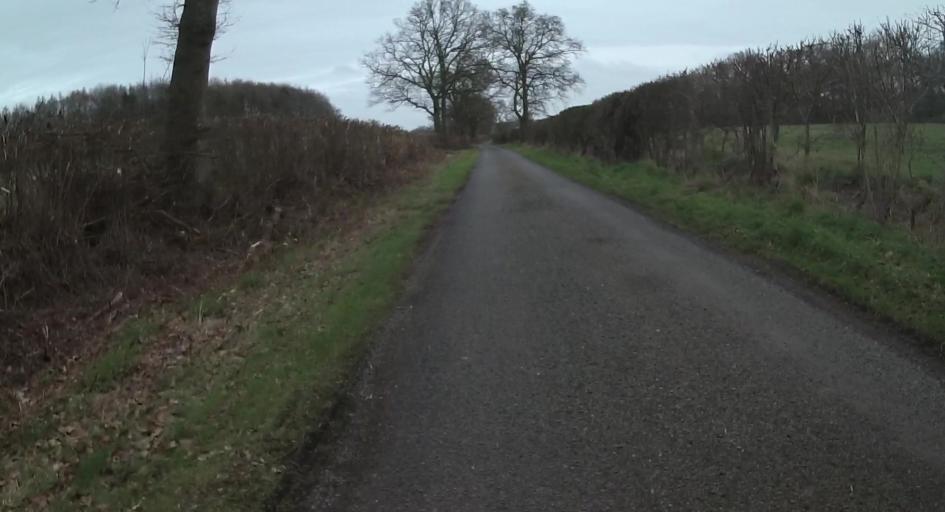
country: GB
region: England
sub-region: Hampshire
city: Overton
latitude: 51.2663
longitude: -1.2471
